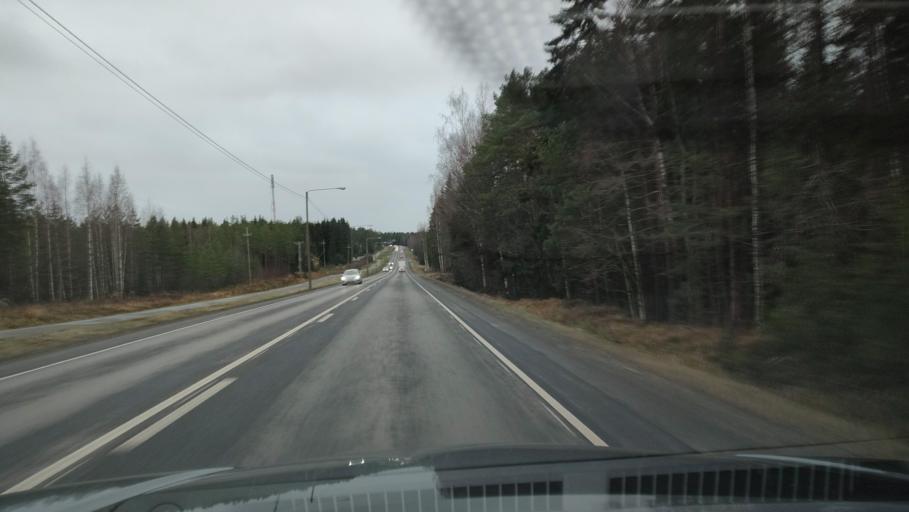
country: FI
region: Southern Ostrobothnia
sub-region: Seinaejoki
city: Seinaejoki
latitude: 62.7806
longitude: 22.7021
